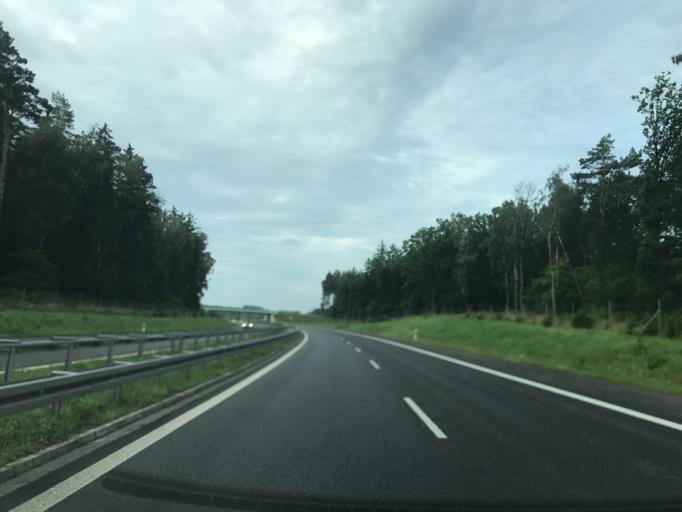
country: PL
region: West Pomeranian Voivodeship
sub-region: Powiat goleniowski
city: Nowogard
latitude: 53.6687
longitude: 15.0768
